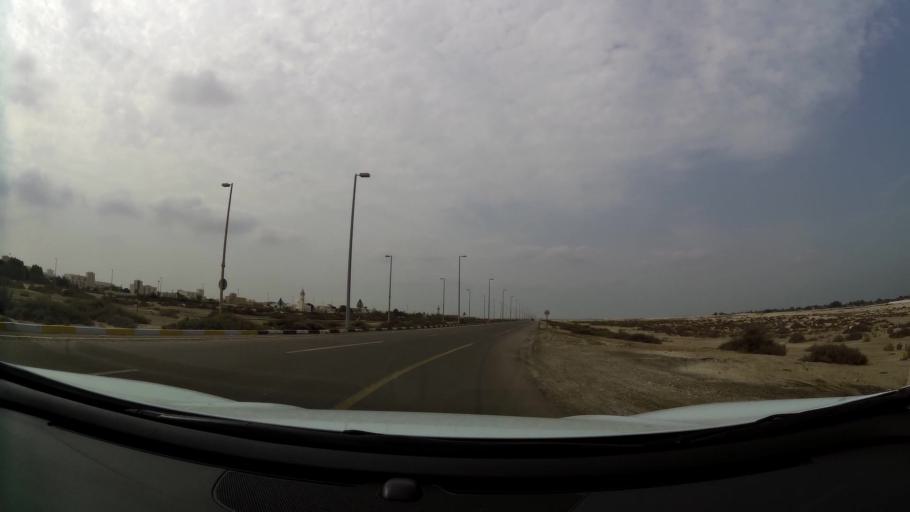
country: AE
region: Abu Dhabi
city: Abu Dhabi
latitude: 24.6508
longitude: 54.6770
